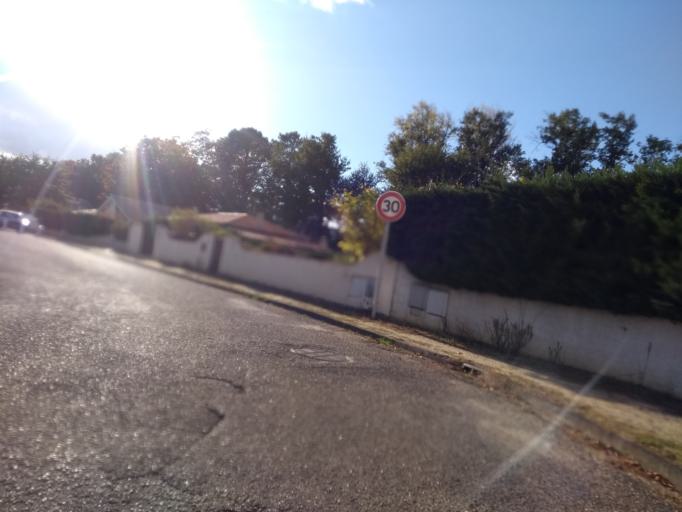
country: FR
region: Aquitaine
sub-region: Departement de la Gironde
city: Cestas
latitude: 44.7200
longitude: -0.6865
